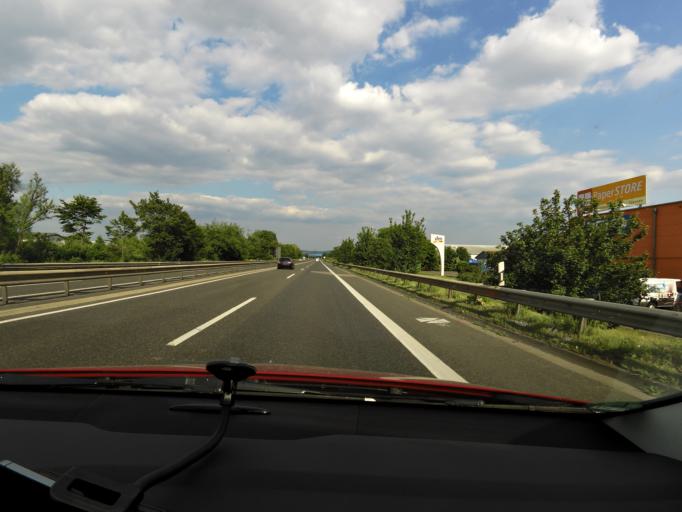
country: DE
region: Rheinland-Pfalz
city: Urmitz
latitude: 50.3972
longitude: 7.5243
